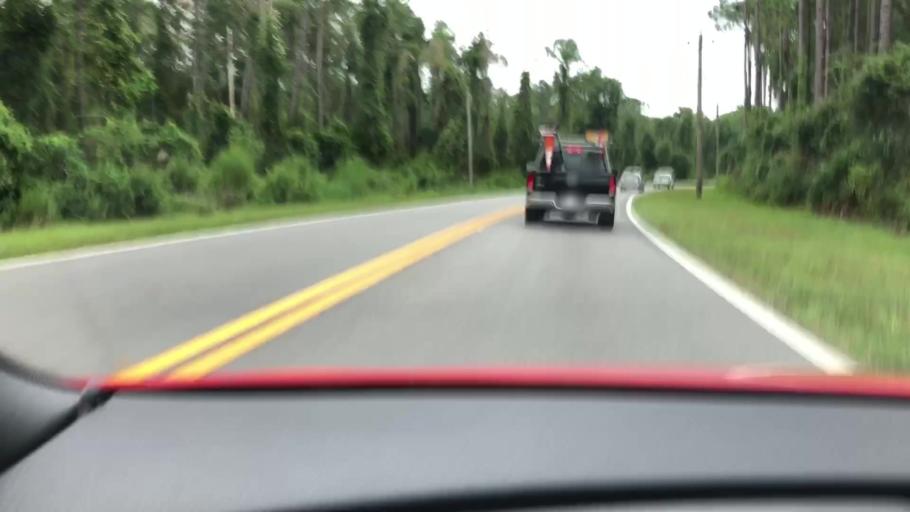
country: US
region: Florida
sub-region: Flagler County
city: Flagler Beach
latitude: 29.5091
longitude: -81.1931
